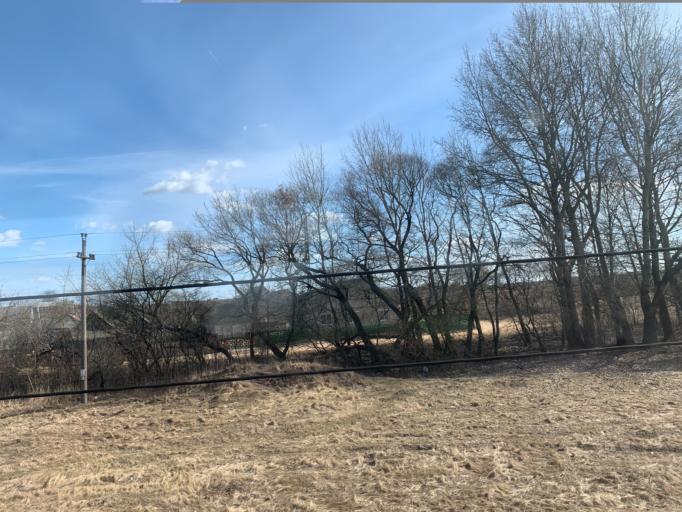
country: BY
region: Minsk
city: Stowbtsy
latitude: 53.4724
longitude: 26.7380
